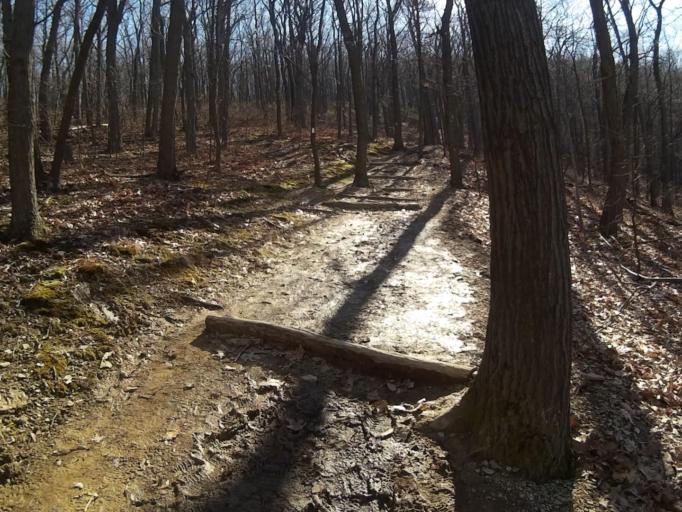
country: US
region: Pennsylvania
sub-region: Centre County
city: Lemont
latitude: 40.8117
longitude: -77.8022
